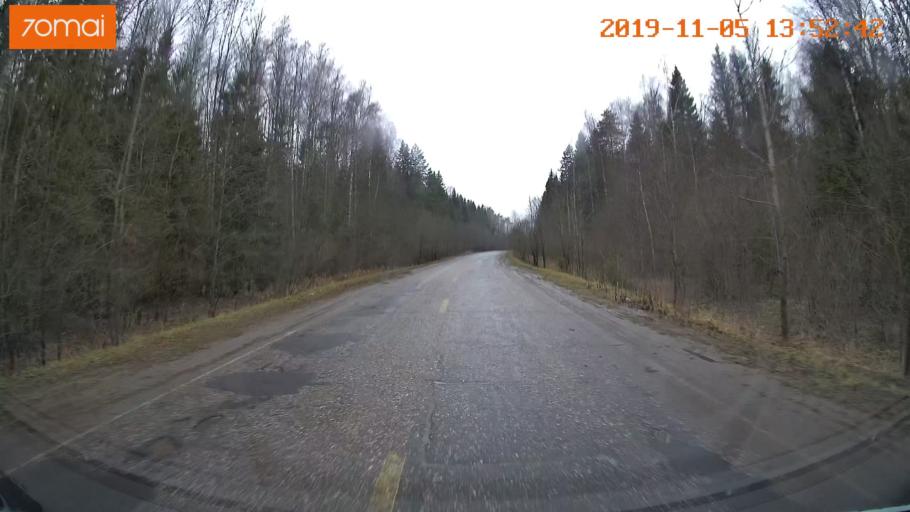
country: RU
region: Ivanovo
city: Kaminskiy
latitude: 57.0286
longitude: 41.3821
